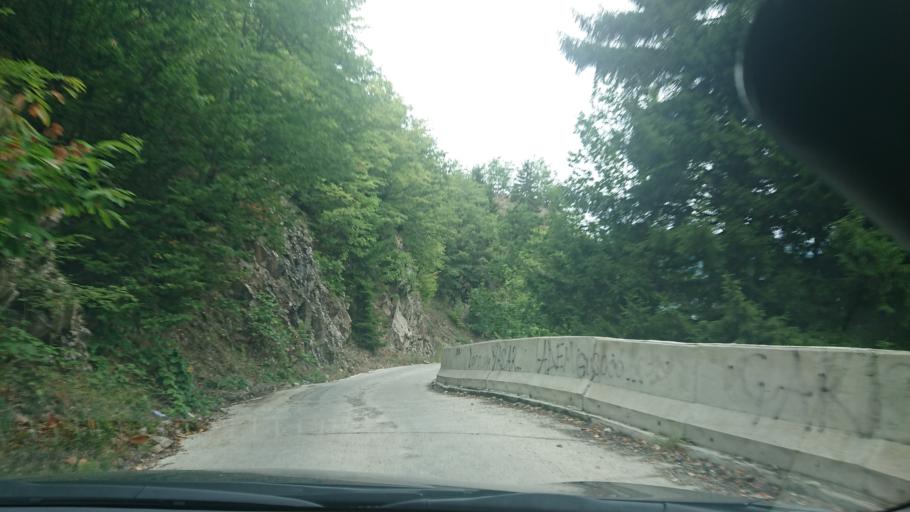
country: TR
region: Gumushane
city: Kurtun
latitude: 40.6841
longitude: 39.0500
